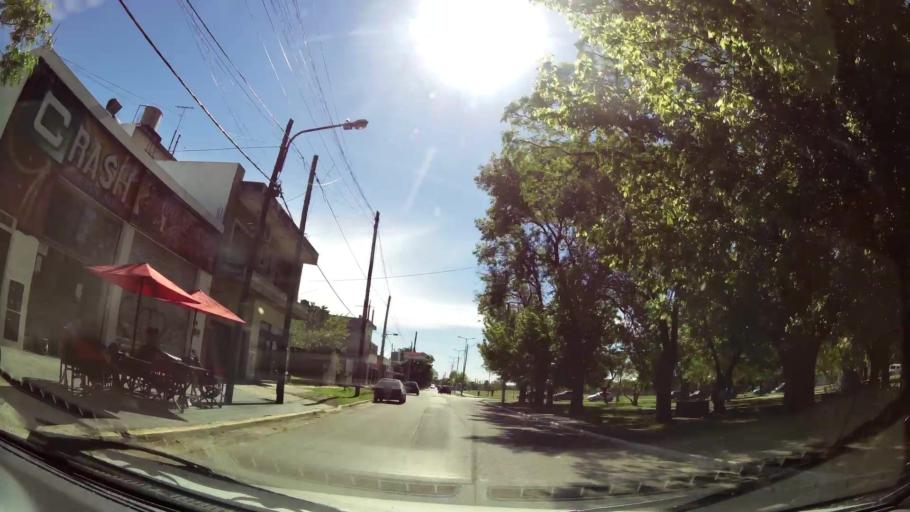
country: AR
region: Buenos Aires
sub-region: Partido de Almirante Brown
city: Adrogue
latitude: -34.7977
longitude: -58.3589
